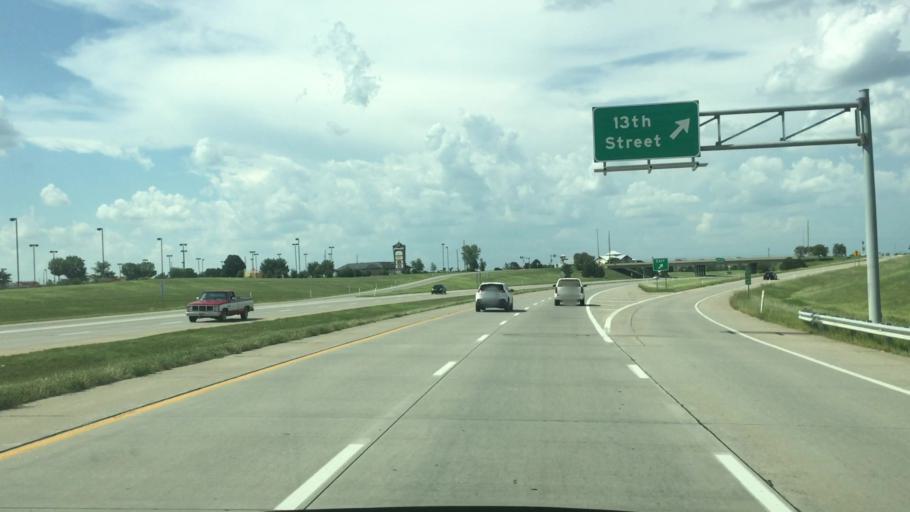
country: US
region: Kansas
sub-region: Butler County
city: Andover
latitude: 37.7046
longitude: -97.1997
